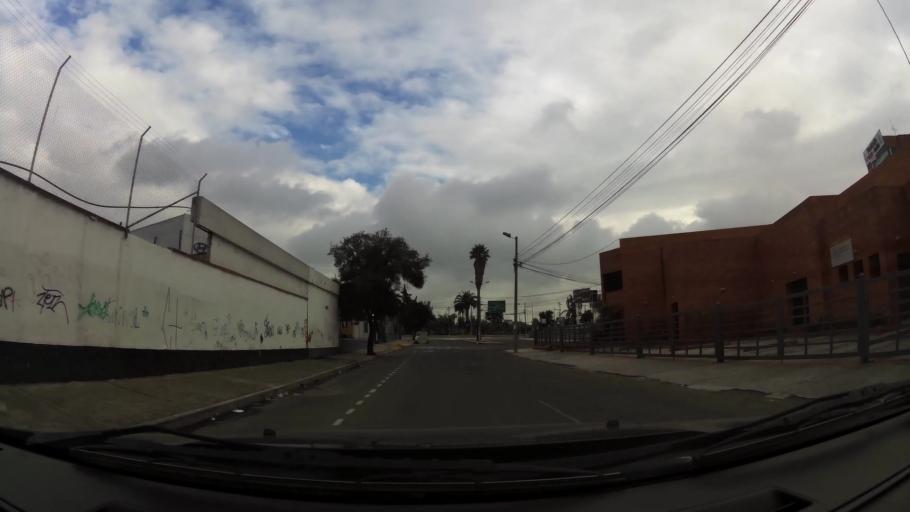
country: EC
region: Pichincha
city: Quito
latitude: -0.1693
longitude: -78.4863
